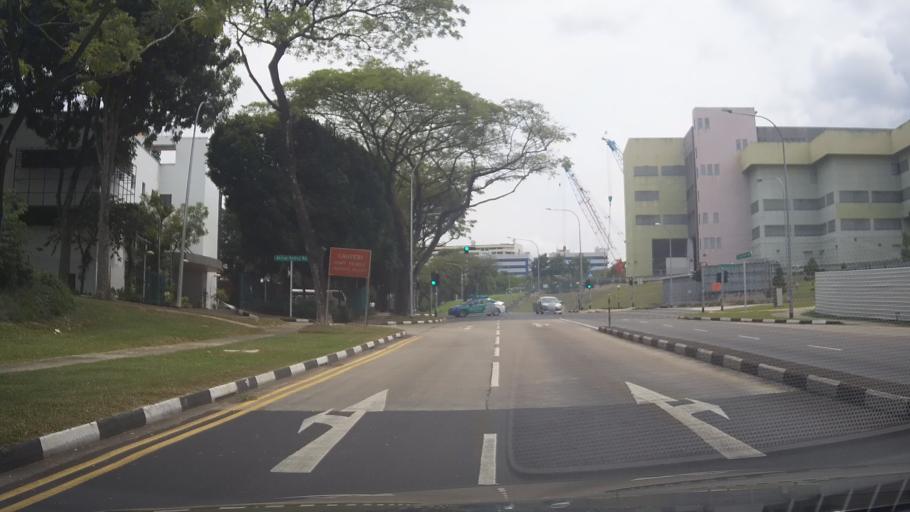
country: MY
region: Johor
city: Johor Bahru
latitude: 1.4581
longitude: 103.7945
